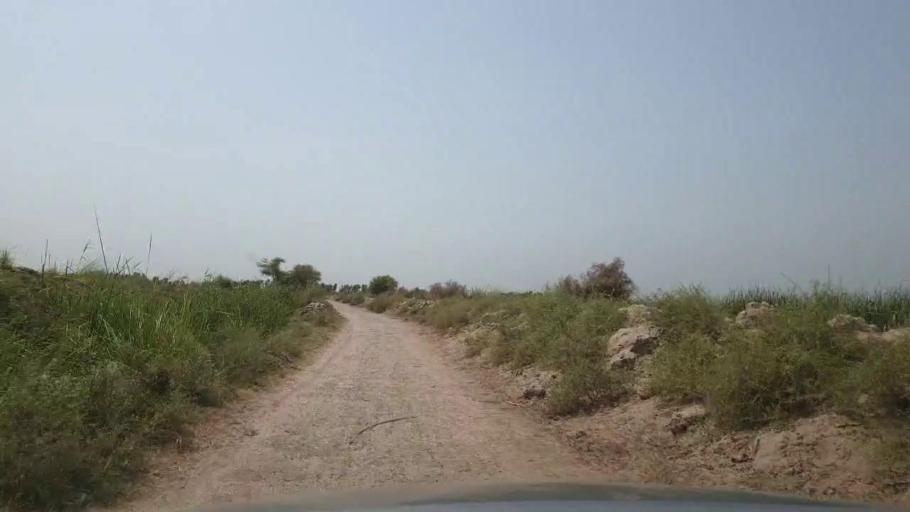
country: PK
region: Sindh
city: Garhi Yasin
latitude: 27.8892
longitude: 68.4594
